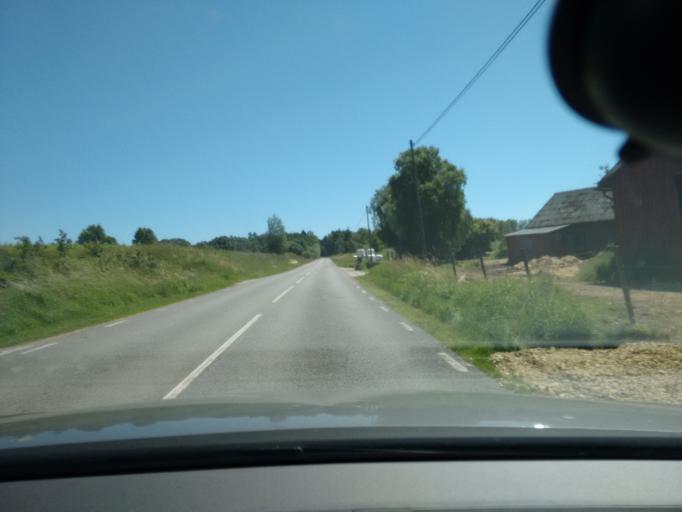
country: SE
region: Skane
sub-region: Kristianstads Kommun
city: Degeberga
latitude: 55.7608
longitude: 13.9162
